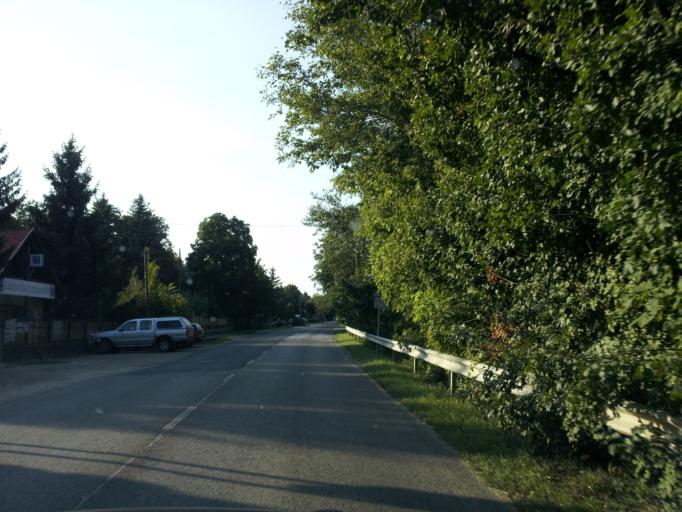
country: HU
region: Pest
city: Tahitotfalu
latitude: 47.7573
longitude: 19.0728
